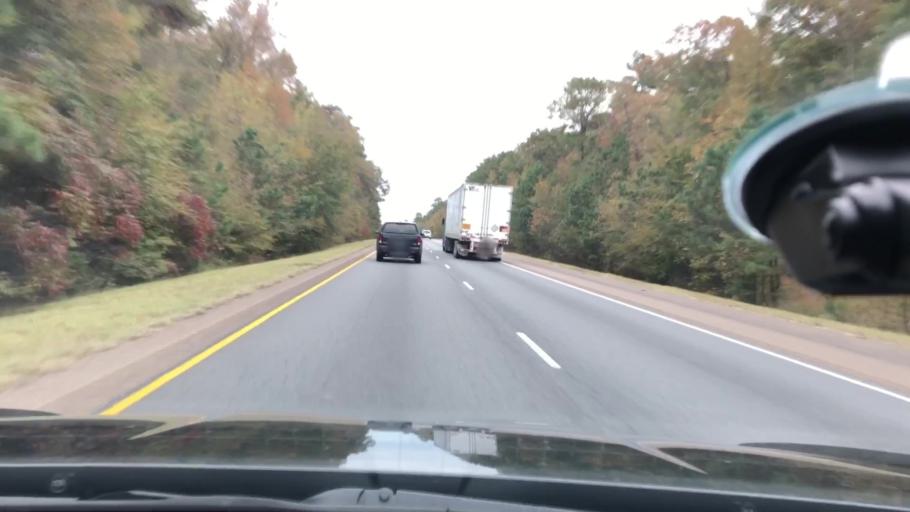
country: US
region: Arkansas
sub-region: Clark County
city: Gurdon
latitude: 33.9202
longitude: -93.2738
